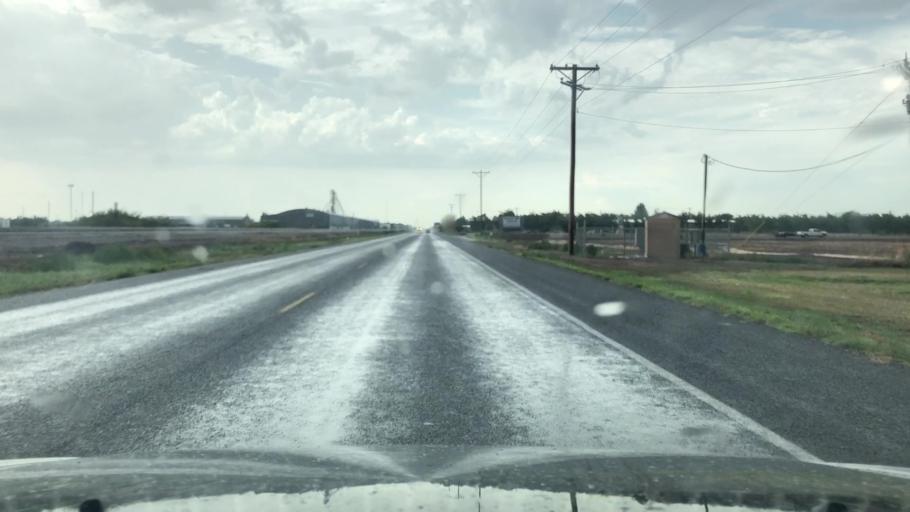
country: US
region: New Mexico
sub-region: Dona Ana County
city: Mesquite
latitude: 32.1576
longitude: -106.6922
